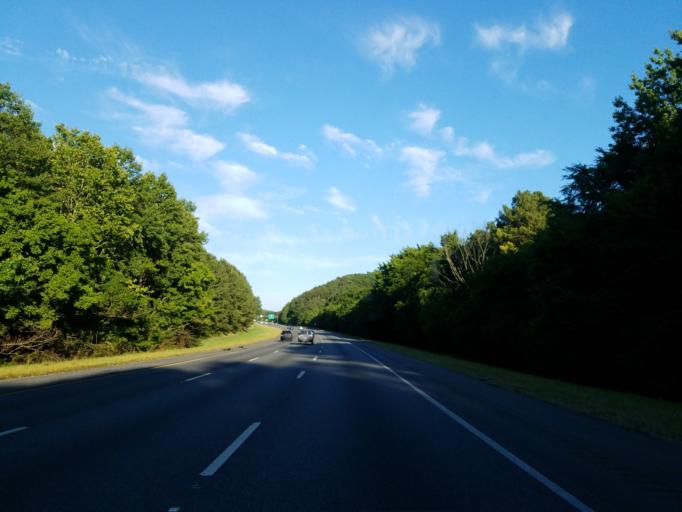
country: US
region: Georgia
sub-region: Bartow County
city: Cartersville
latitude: 34.2503
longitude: -84.7854
